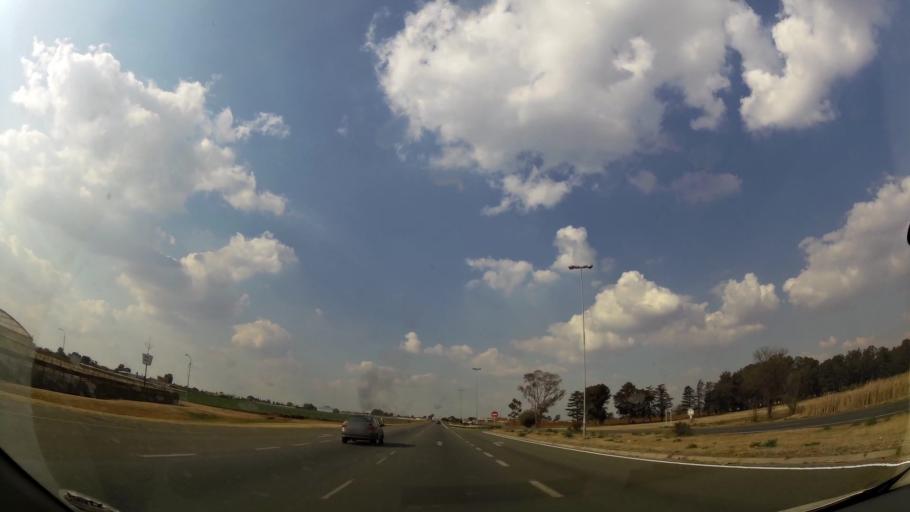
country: ZA
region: Gauteng
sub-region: Ekurhuleni Metropolitan Municipality
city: Germiston
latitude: -26.2917
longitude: 28.2226
